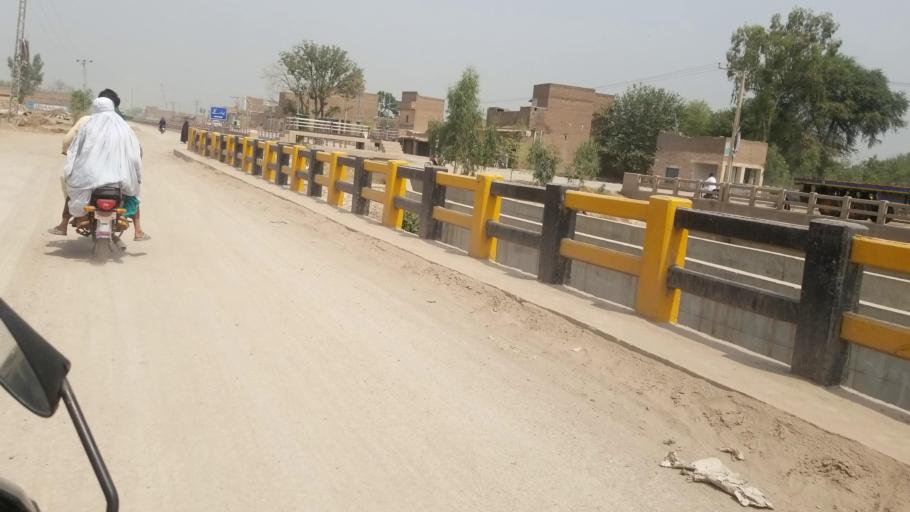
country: PK
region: Khyber Pakhtunkhwa
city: Peshawar
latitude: 33.9634
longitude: 71.5420
